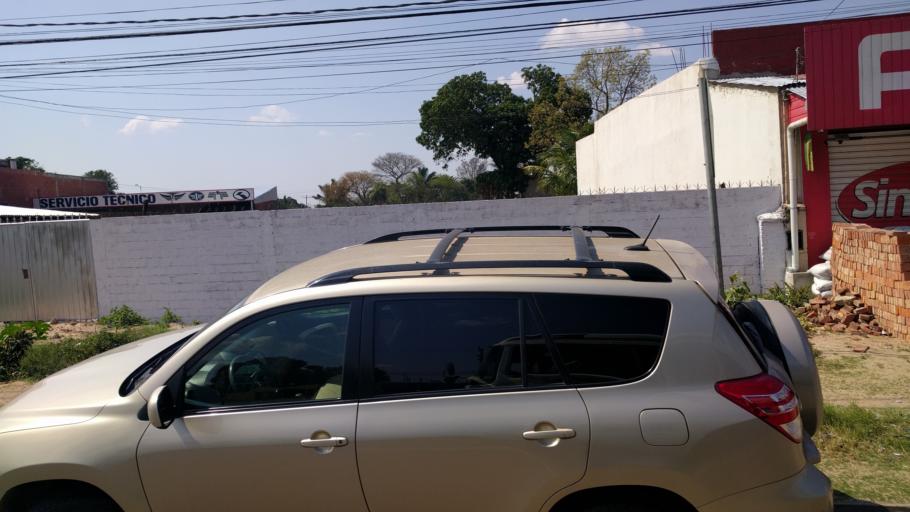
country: BO
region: Santa Cruz
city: Santa Cruz de la Sierra
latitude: -17.7210
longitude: -63.1638
